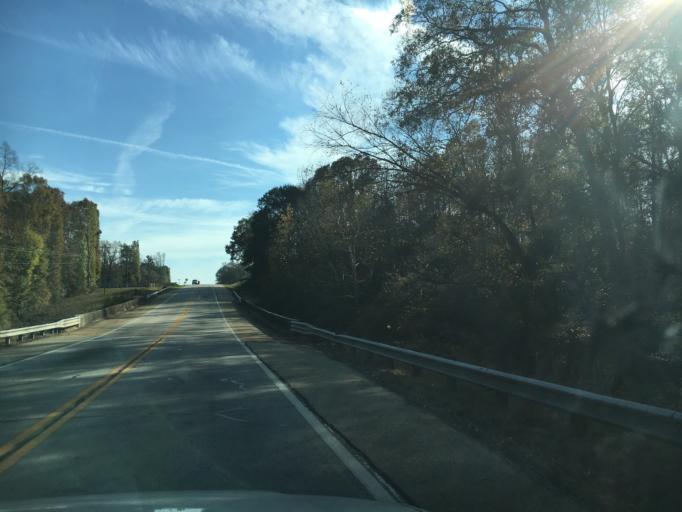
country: US
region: Georgia
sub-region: Hart County
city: Hartwell
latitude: 34.2460
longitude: -82.8999
